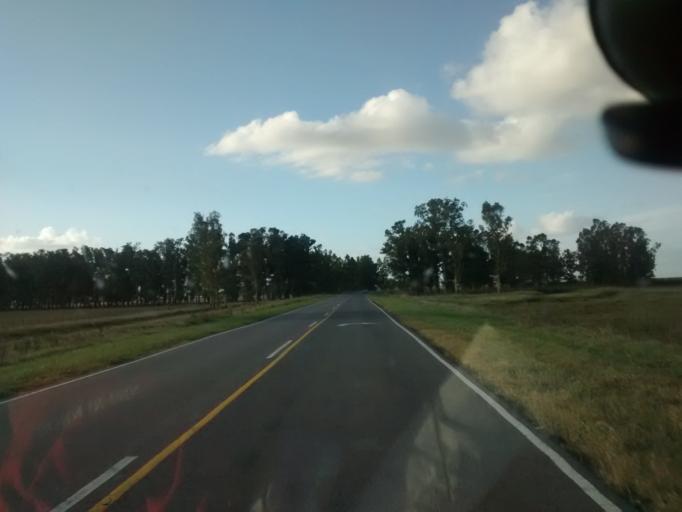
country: AR
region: Buenos Aires
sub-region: Partido de General Belgrano
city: General Belgrano
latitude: -36.1485
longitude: -58.5954
